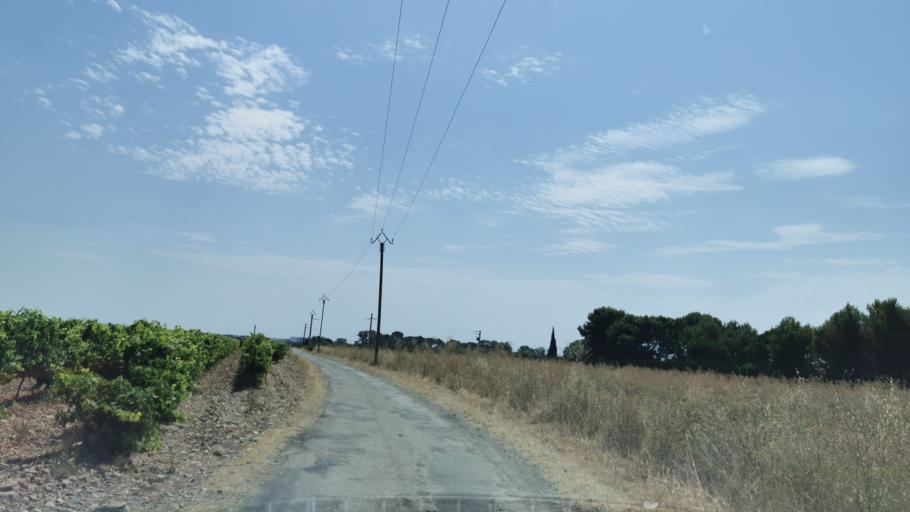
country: FR
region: Languedoc-Roussillon
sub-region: Departement de l'Aude
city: Argeliers
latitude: 43.2892
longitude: 2.8926
